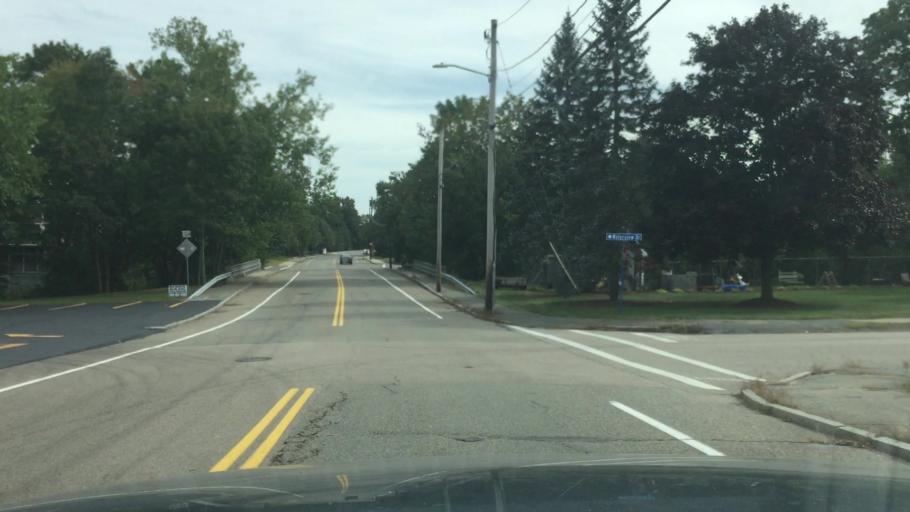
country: US
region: Massachusetts
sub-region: Norfolk County
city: Medway
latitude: 42.1389
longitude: -71.4314
